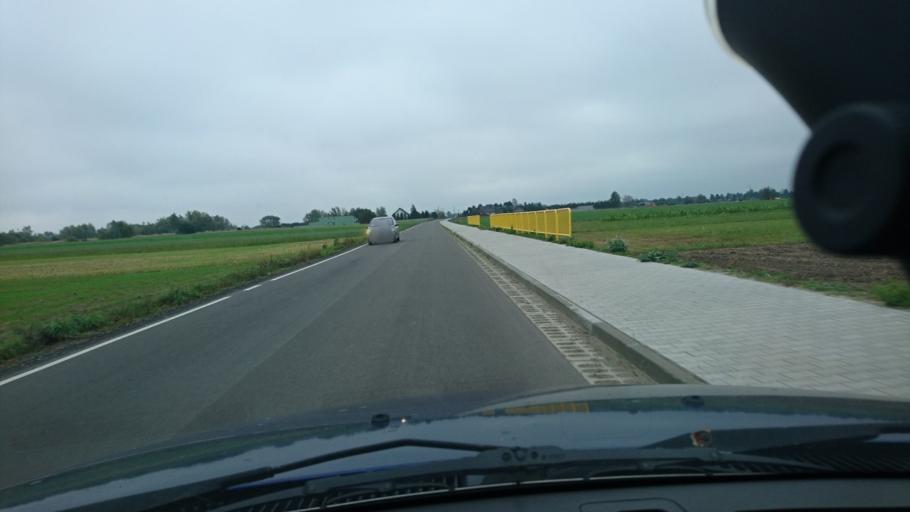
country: PL
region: Greater Poland Voivodeship
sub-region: Powiat ostrowski
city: Odolanow
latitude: 51.5737
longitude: 17.6054
